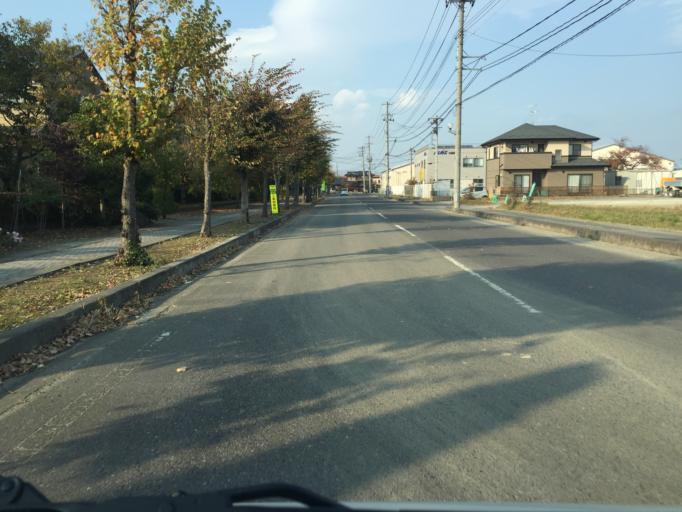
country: JP
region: Fukushima
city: Motomiya
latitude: 37.5106
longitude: 140.3981
